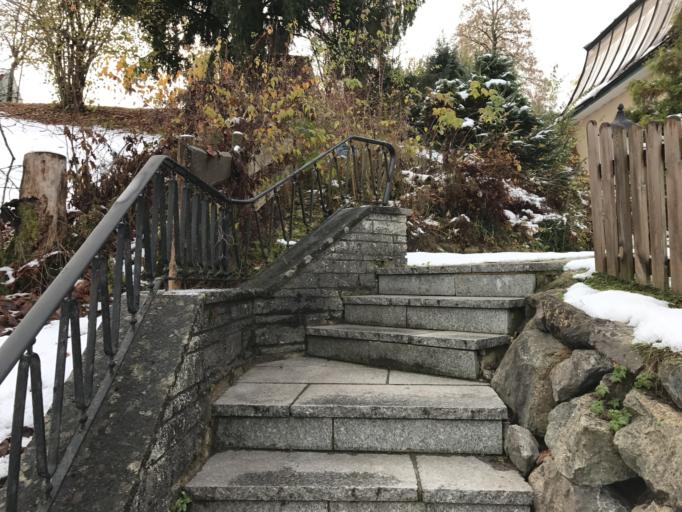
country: DE
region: Bavaria
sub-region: Swabia
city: Weiler-Simmerberg
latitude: 47.5800
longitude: 9.9187
